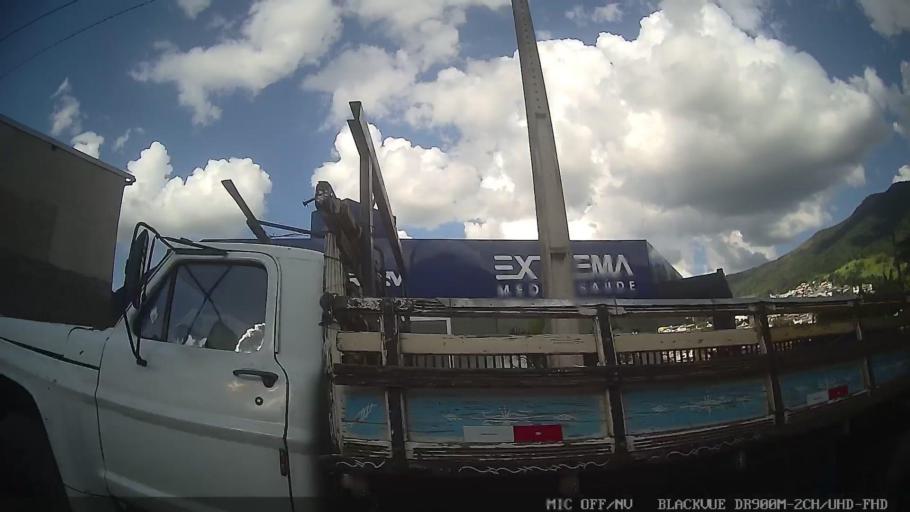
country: BR
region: Minas Gerais
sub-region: Extrema
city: Extrema
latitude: -22.8584
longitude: -46.3255
